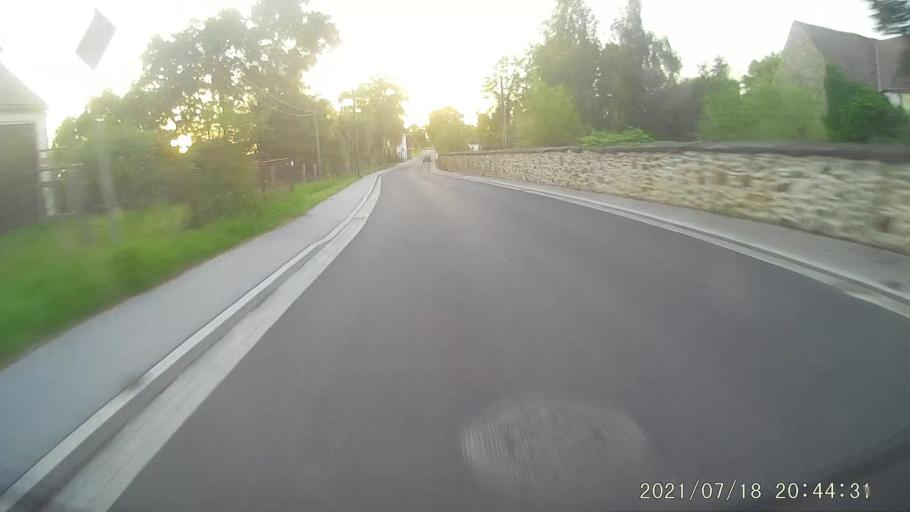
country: DE
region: Saxony
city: Reichenbach
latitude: 51.1976
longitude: 14.7759
